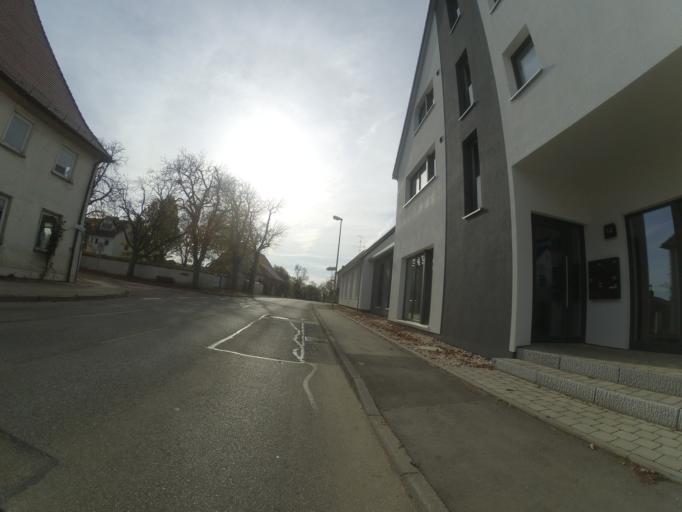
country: DE
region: Baden-Wuerttemberg
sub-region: Tuebingen Region
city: Blaubeuren
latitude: 48.4260
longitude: 9.8642
